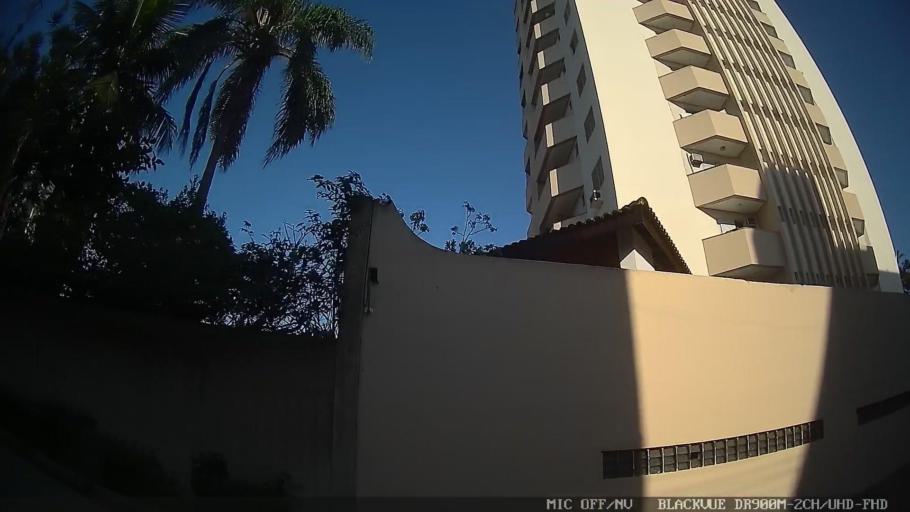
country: BR
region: Sao Paulo
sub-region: Guaruja
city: Guaruja
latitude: -24.0117
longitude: -46.2771
